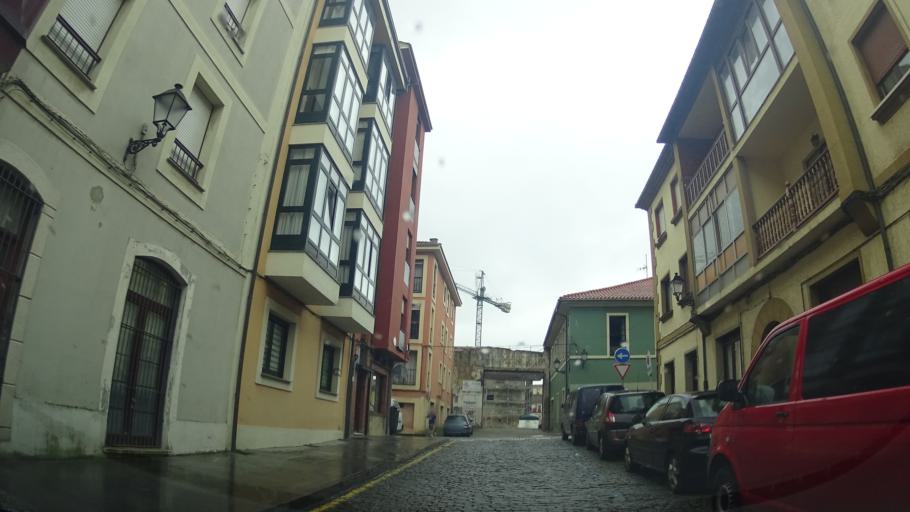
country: ES
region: Asturias
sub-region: Province of Asturias
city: Gijon
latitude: 43.5468
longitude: -5.6616
